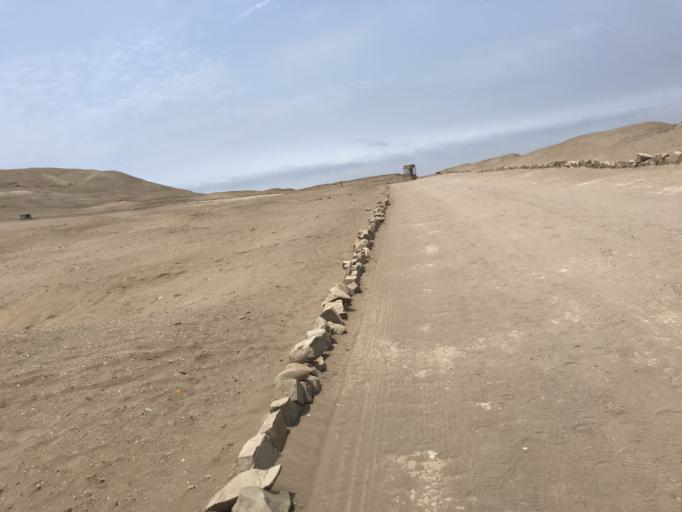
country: PE
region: Lima
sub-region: Lima
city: Punta Hermosa
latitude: -12.2598
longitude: -76.9015
